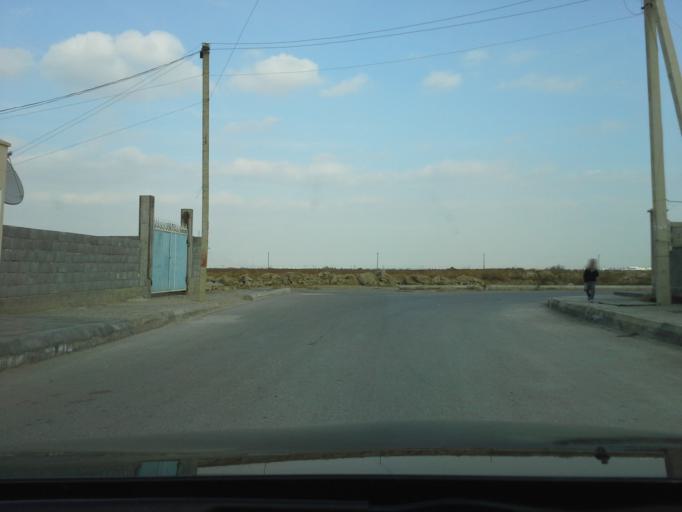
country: TM
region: Ahal
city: Abadan
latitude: 38.0448
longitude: 58.2740
